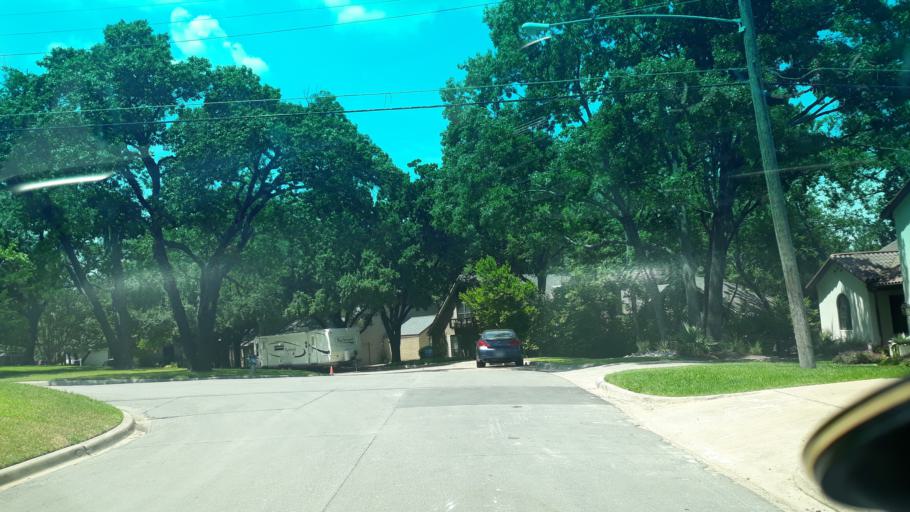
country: US
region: Texas
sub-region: Dallas County
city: Highland Park
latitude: 32.8259
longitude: -96.7386
